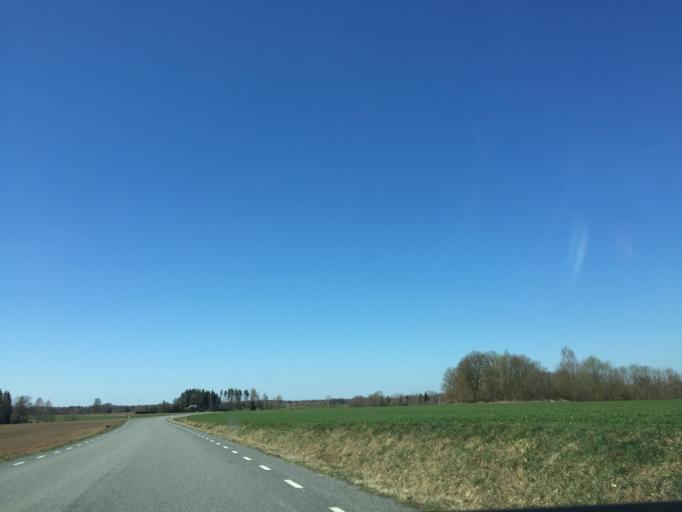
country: EE
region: Viljandimaa
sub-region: Viiratsi vald
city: Viiratsi
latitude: 58.3562
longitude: 25.7357
